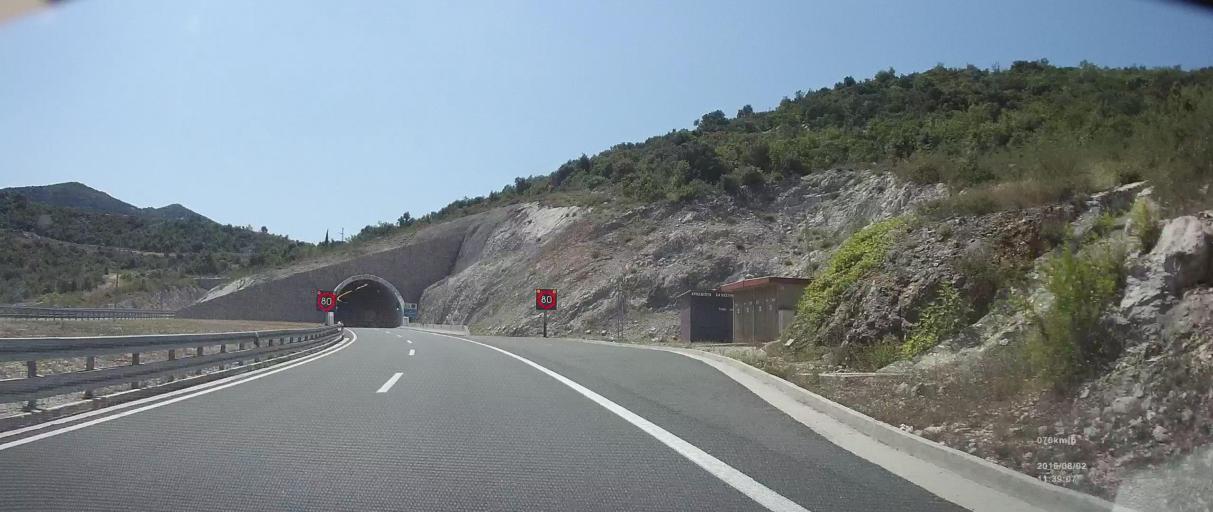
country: HR
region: Dubrovacko-Neretvanska
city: Komin
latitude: 43.0889
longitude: 17.4895
